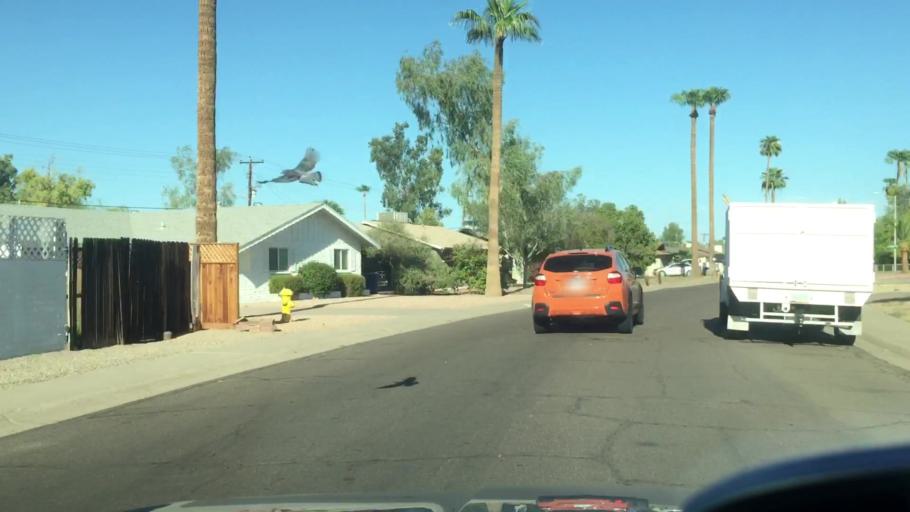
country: US
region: Arizona
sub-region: Maricopa County
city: Tempe
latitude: 33.4050
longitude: -111.9077
